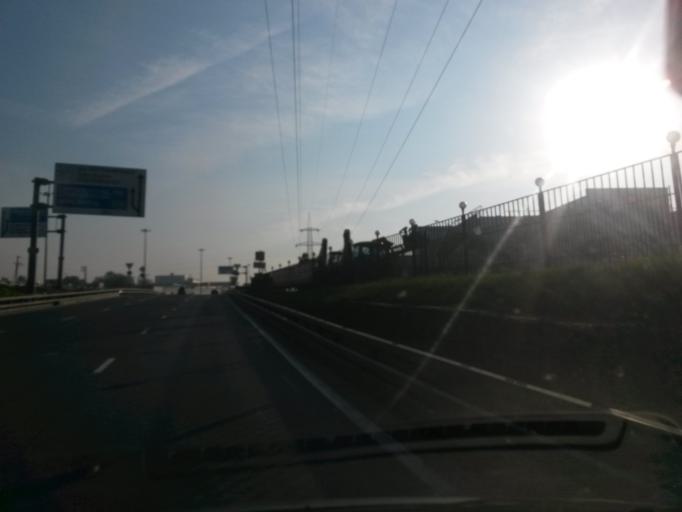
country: RU
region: Moskovskaya
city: Druzhba
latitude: 55.8838
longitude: 37.7307
